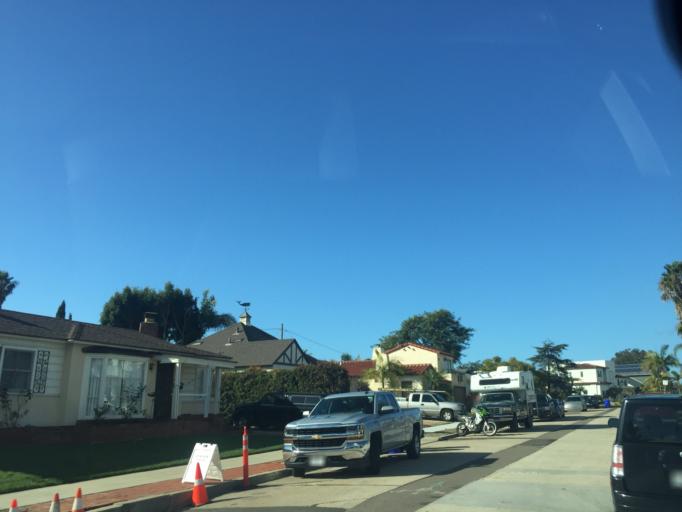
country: US
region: California
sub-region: San Diego County
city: La Jolla
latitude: 32.7813
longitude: -117.2369
